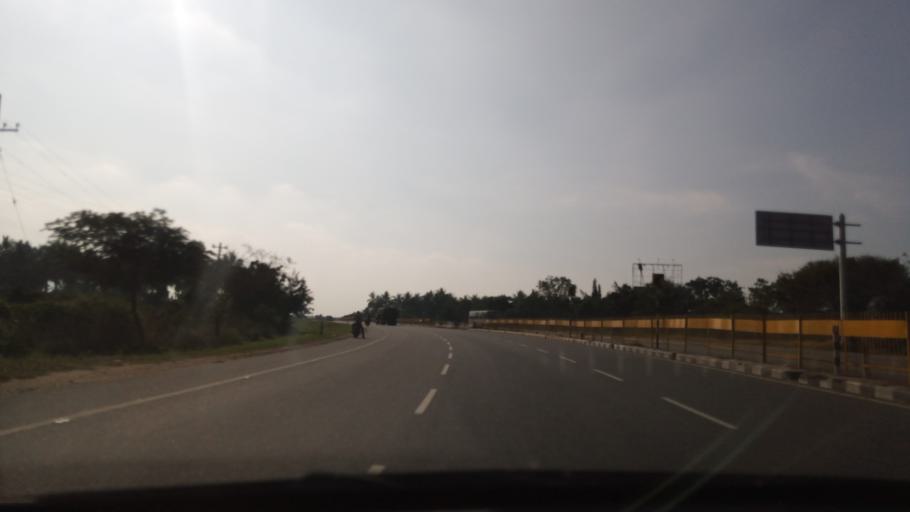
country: IN
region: Tamil Nadu
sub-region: Krishnagiri
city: Krishnagiri
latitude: 12.5477
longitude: 78.3274
